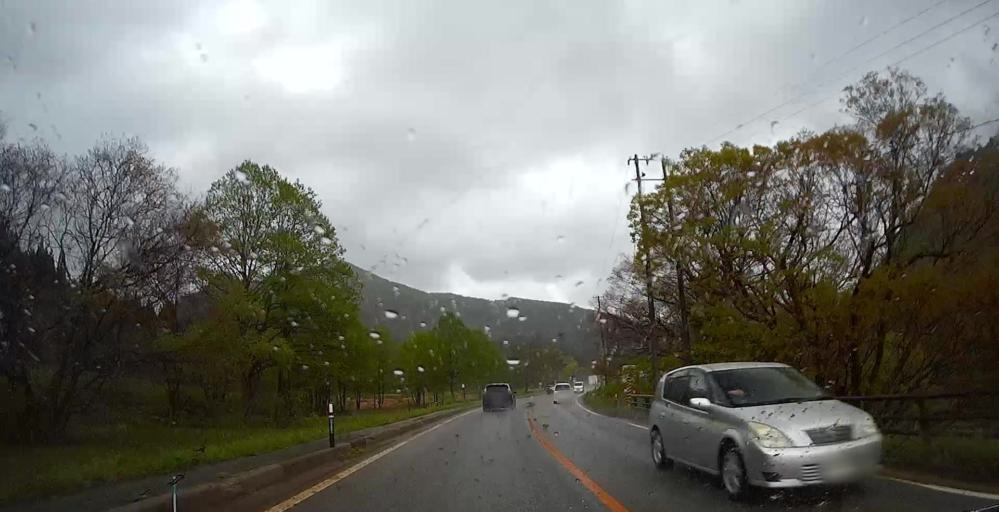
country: JP
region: Yamagata
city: Nagai
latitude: 38.0529
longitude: 139.8139
